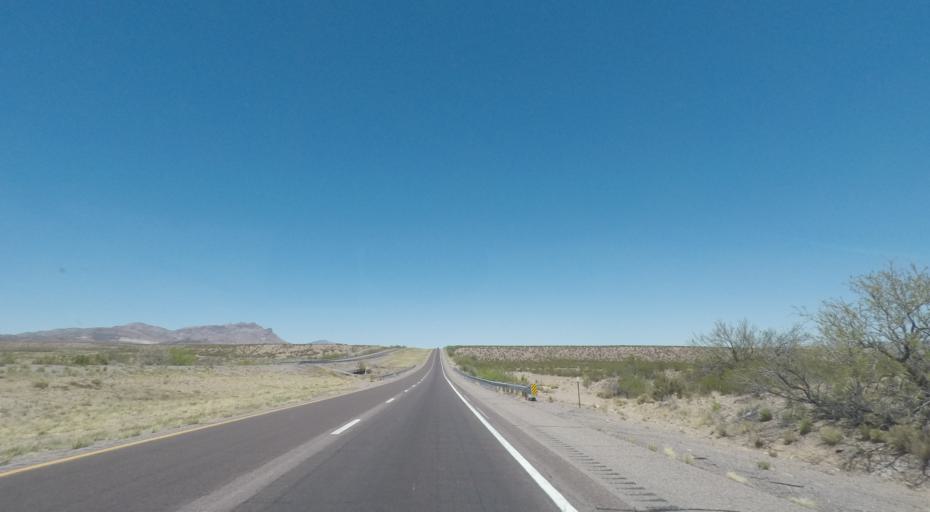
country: US
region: New Mexico
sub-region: Socorro County
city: Socorro
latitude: 33.9722
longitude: -106.8896
